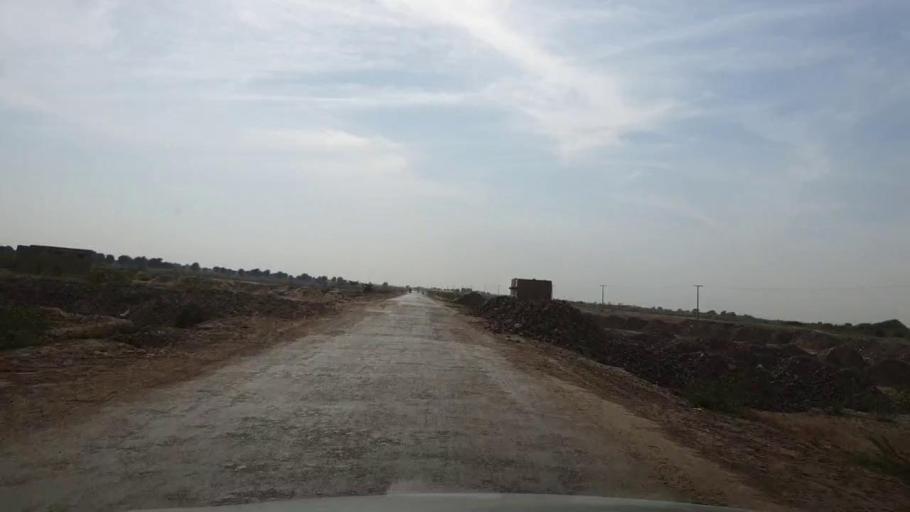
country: PK
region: Sindh
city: Kunri
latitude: 25.1686
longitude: 69.5198
